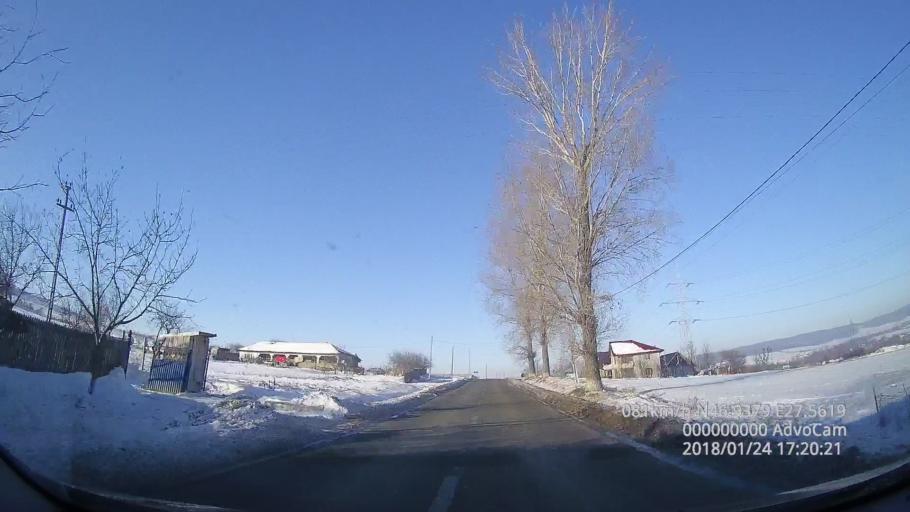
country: RO
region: Iasi
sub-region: Comuna Scanteia
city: Scanteia
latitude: 46.9385
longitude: 27.5617
